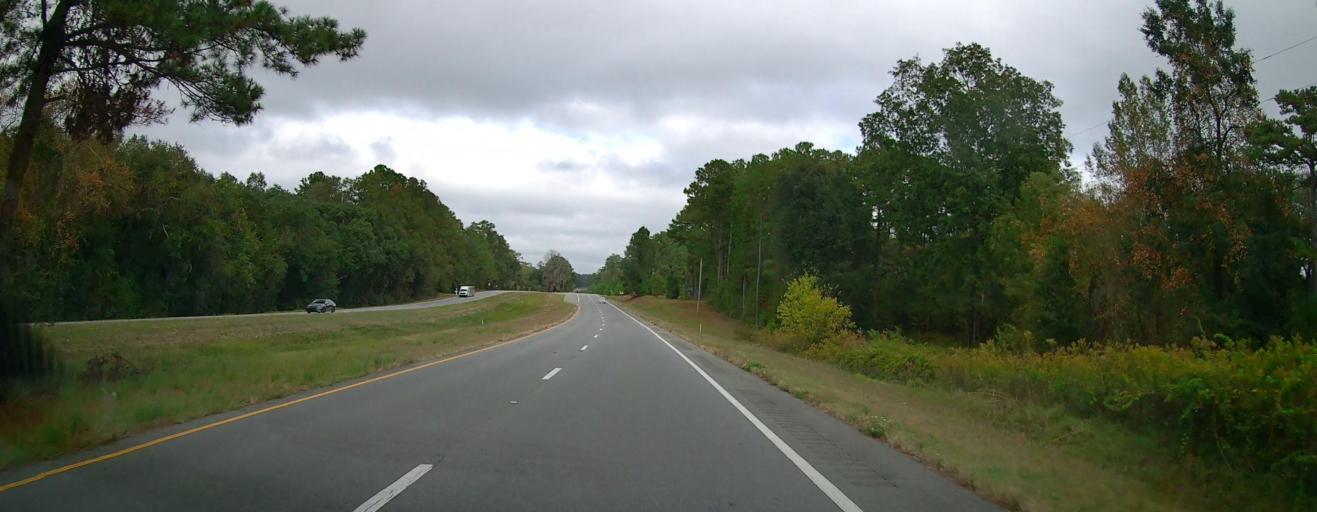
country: US
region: Georgia
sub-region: Grady County
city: Cairo
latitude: 30.6864
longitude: -84.1510
